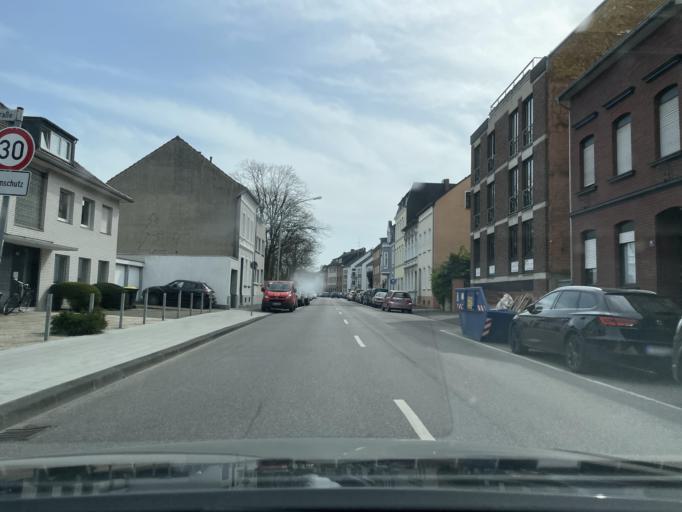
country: DE
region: North Rhine-Westphalia
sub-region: Regierungsbezirk Dusseldorf
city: Monchengladbach
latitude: 51.2036
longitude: 6.4135
